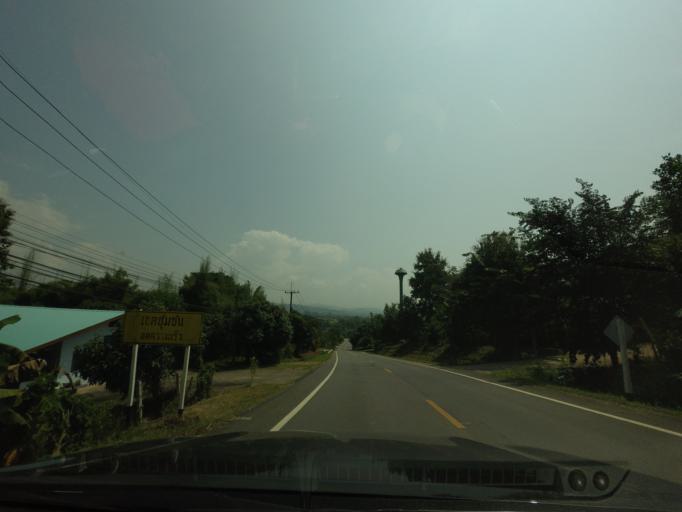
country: TH
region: Nan
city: Santi Suk
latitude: 18.9238
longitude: 100.9215
